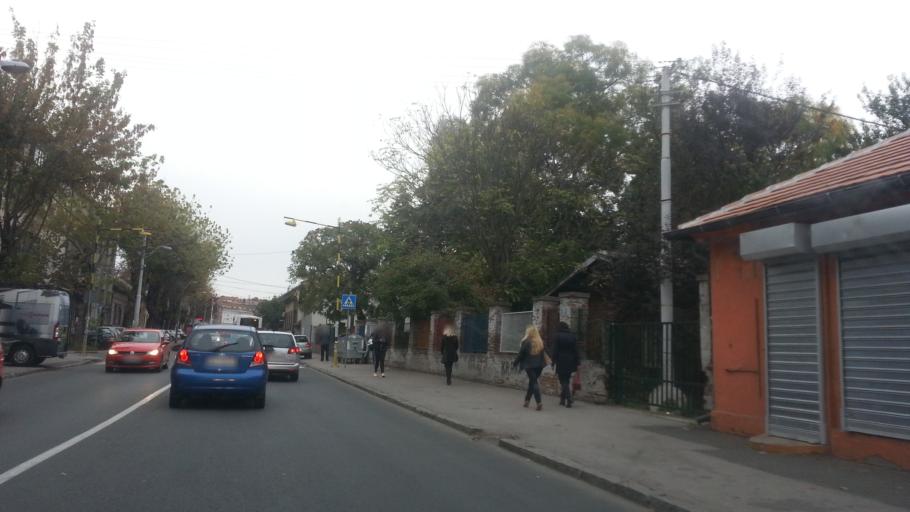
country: RS
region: Central Serbia
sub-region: Belgrade
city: Zemun
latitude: 44.8392
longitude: 20.4033
